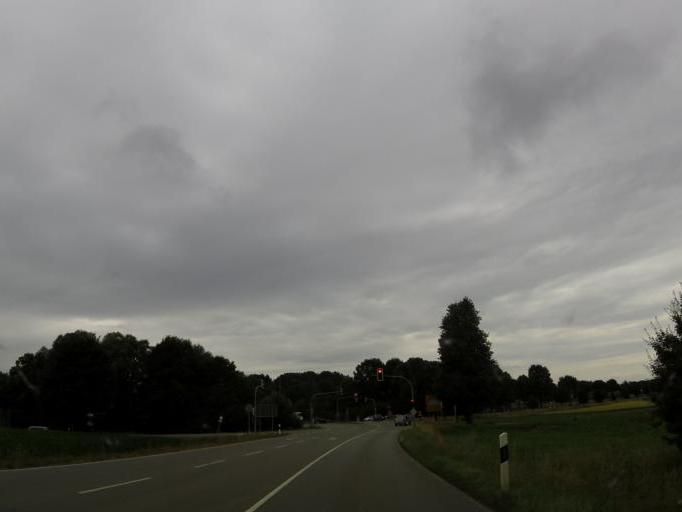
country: DE
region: Bavaria
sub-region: Upper Bavaria
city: Erding
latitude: 48.2860
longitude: 11.9130
